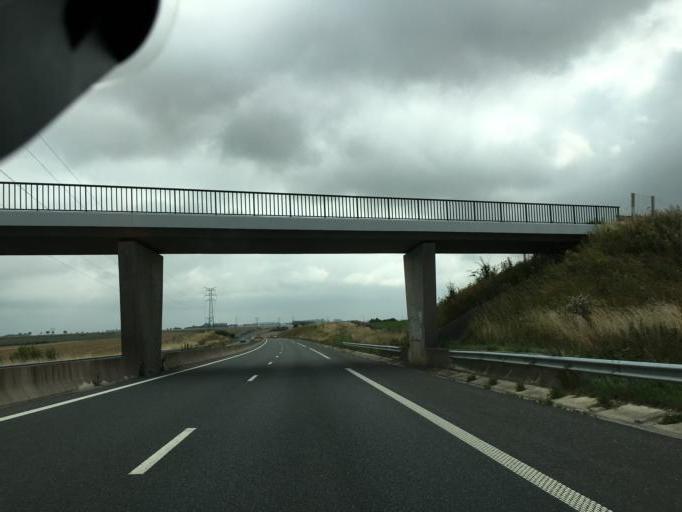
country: FR
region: Nord-Pas-de-Calais
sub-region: Departement du Pas-de-Calais
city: Montreuil
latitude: 50.4329
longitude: 1.7462
